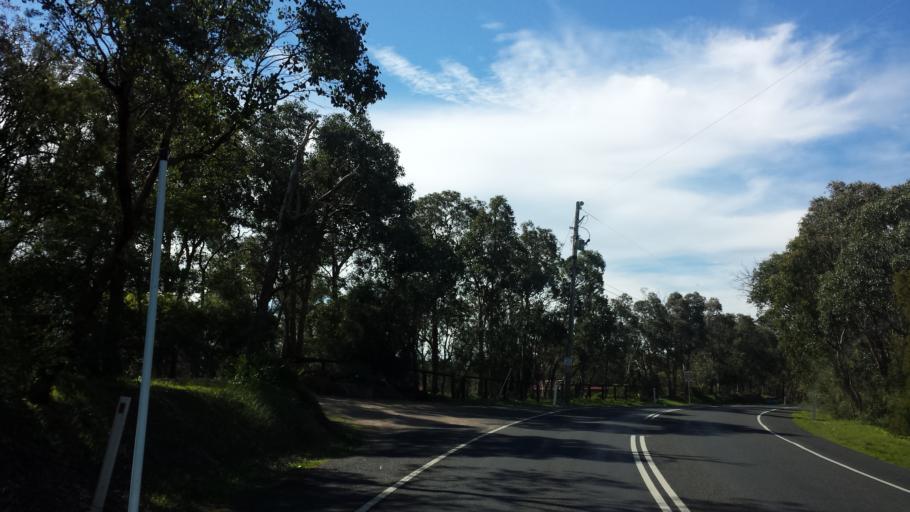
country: AU
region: Victoria
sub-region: Nillumbik
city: North Warrandyte
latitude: -37.7088
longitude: 145.2228
